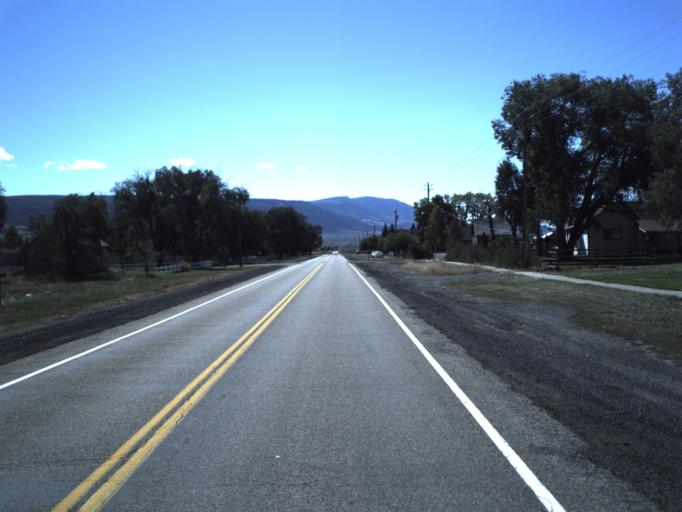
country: US
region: Utah
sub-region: Wayne County
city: Loa
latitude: 38.5096
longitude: -111.8814
